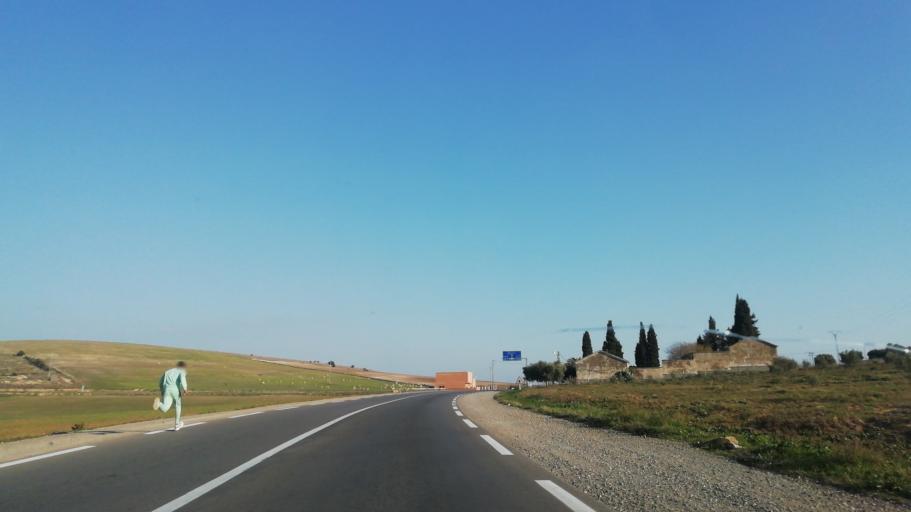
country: DZ
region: Ain Temouchent
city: Hammam Bou Hadjar
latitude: 35.1650
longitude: -0.8770
